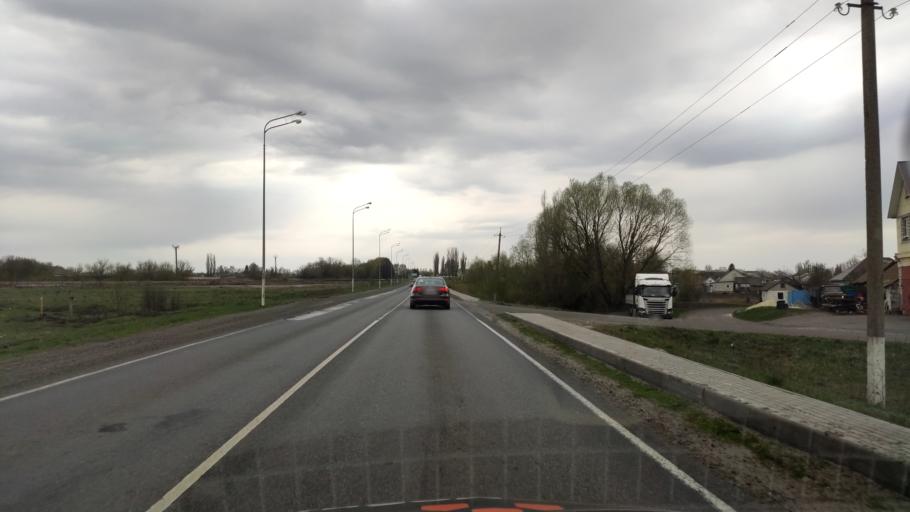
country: RU
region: Kursk
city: Gorshechnoye
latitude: 51.5322
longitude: 38.0224
